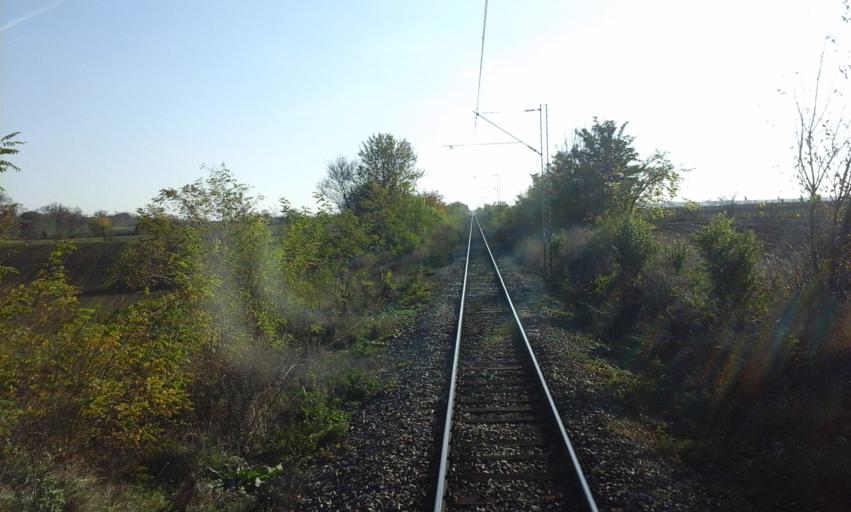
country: RS
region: Autonomna Pokrajina Vojvodina
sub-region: Severnobacki Okrug
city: Mali Igos
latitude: 45.7396
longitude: 19.6491
